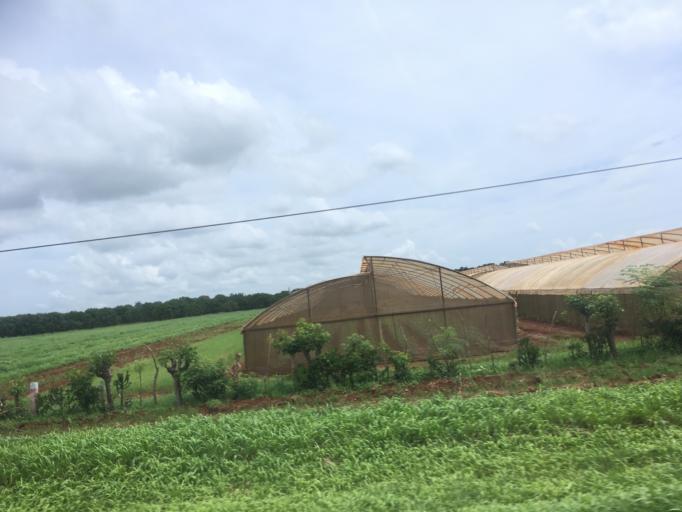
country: CU
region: Matanzas
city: Jovellanos
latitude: 22.7983
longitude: -81.1629
